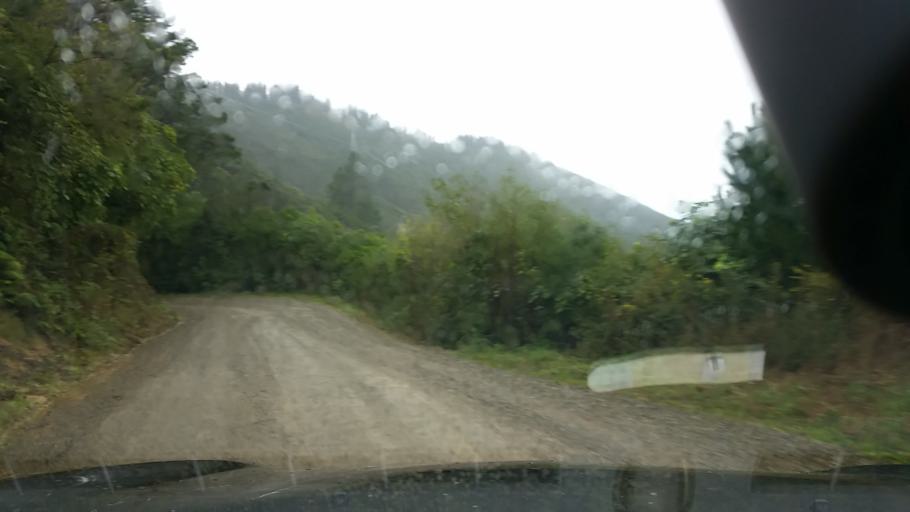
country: NZ
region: Marlborough
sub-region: Marlborough District
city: Picton
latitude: -41.3460
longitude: 174.0727
